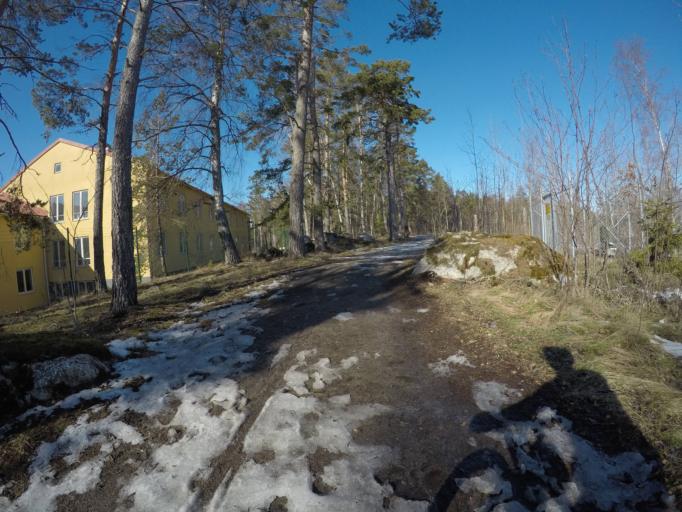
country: SE
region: Vaestmanland
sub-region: Vasteras
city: Vasteras
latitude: 59.5908
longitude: 16.6237
